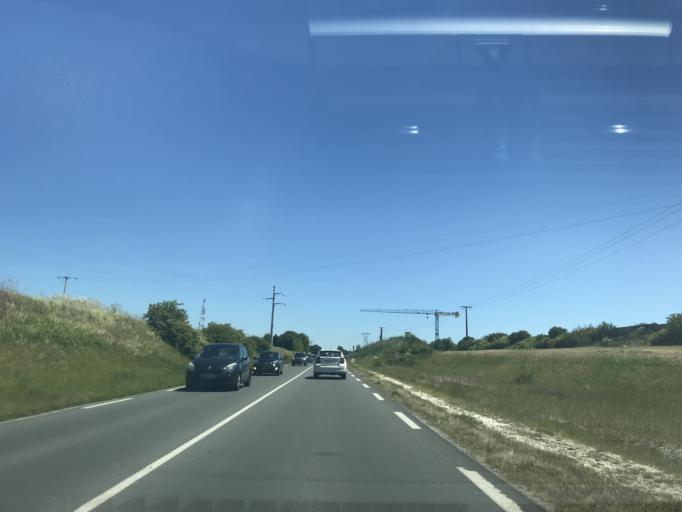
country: FR
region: Poitou-Charentes
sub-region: Departement de la Charente-Maritime
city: Royan
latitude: 45.6432
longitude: -1.0396
